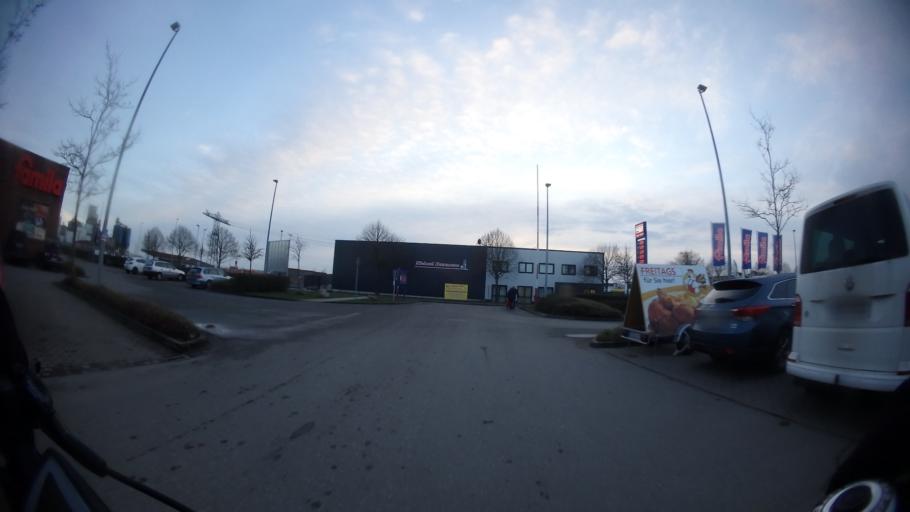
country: DE
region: Mecklenburg-Vorpommern
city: Selmsdorf
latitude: 53.9016
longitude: 10.8066
